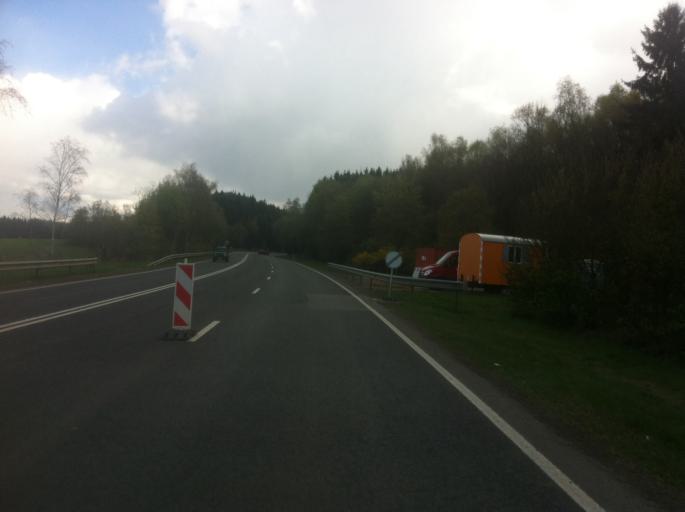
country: LU
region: Diekirch
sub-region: Canton de Wiltz
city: Winseler
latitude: 49.9576
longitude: 5.8626
